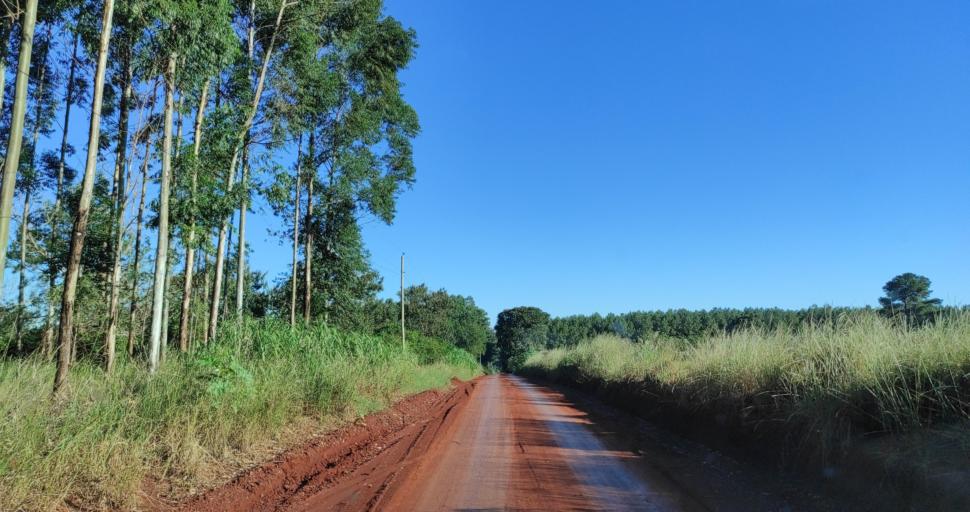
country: AR
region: Misiones
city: Puerto Rico
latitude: -26.8582
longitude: -55.0144
